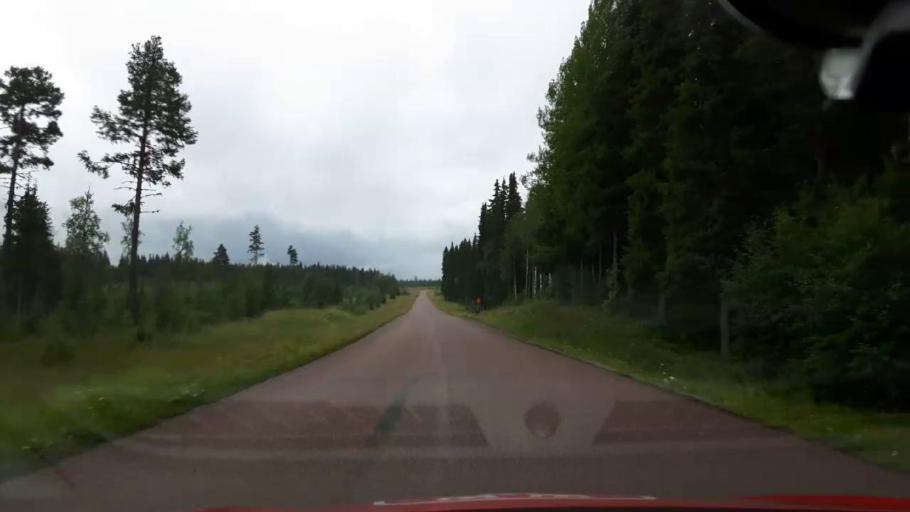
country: SE
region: Jaemtland
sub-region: Krokoms Kommun
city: Valla
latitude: 63.3799
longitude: 13.7587
